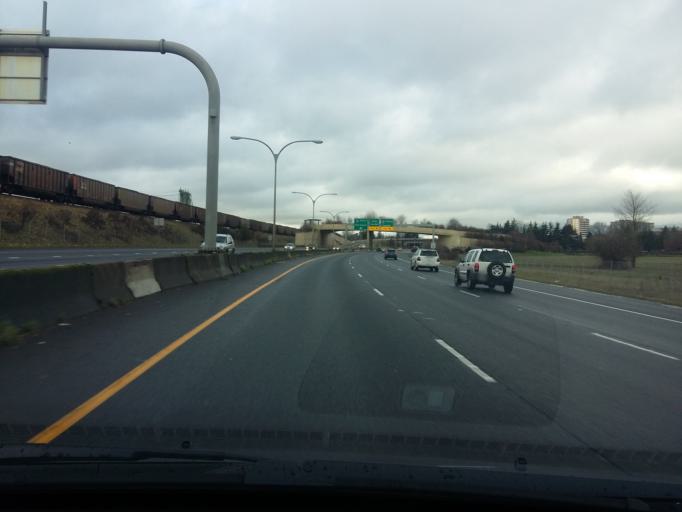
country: US
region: Washington
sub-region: Clark County
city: Vancouver
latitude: 45.6198
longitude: -122.6639
